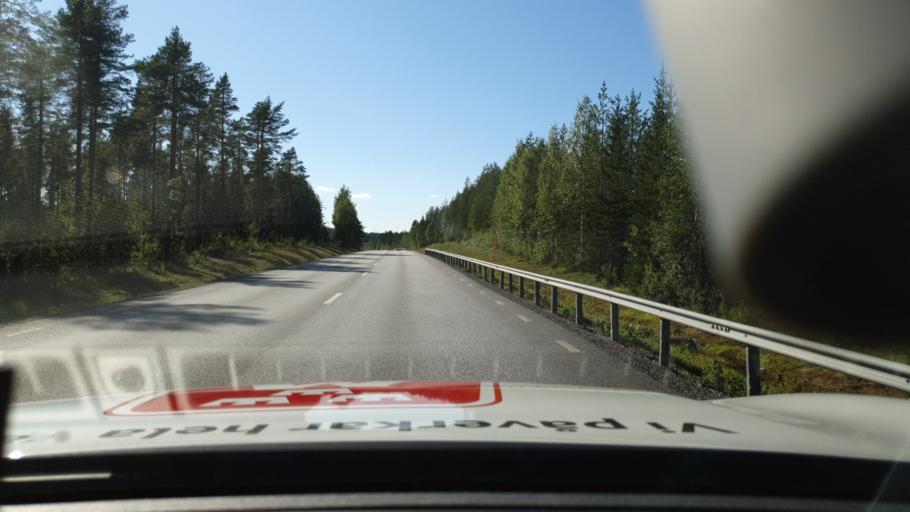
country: SE
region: Norrbotten
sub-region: Pitea Kommun
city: Rosvik
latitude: 65.5963
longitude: 21.6195
